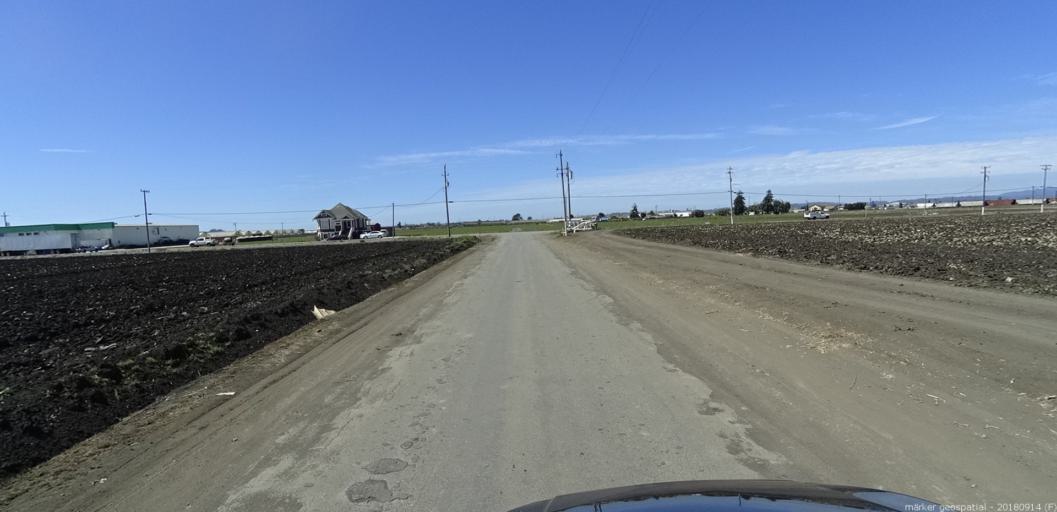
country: US
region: California
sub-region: Monterey County
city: Pajaro
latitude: 36.8942
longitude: -121.7341
